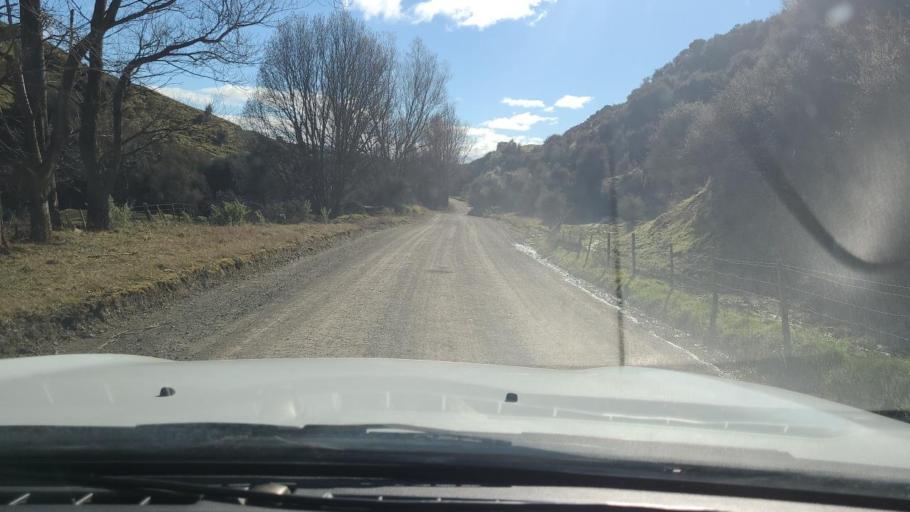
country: NZ
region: Hawke's Bay
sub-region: Napier City
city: Taradale
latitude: -39.2235
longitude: 176.5040
